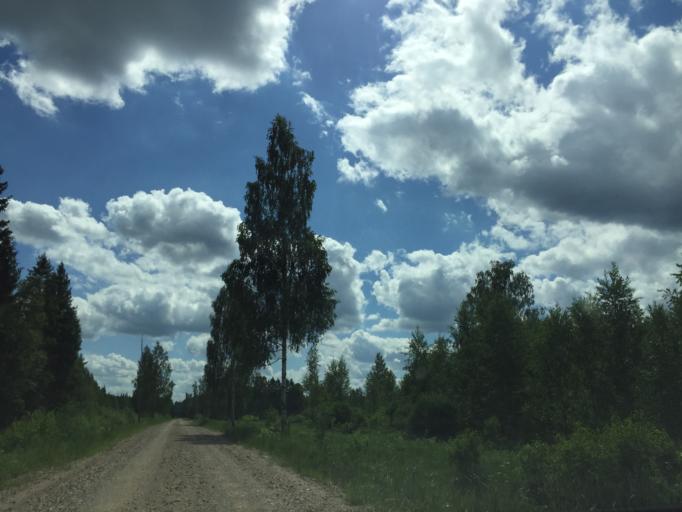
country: LV
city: Tireli
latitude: 56.8562
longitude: 23.6924
